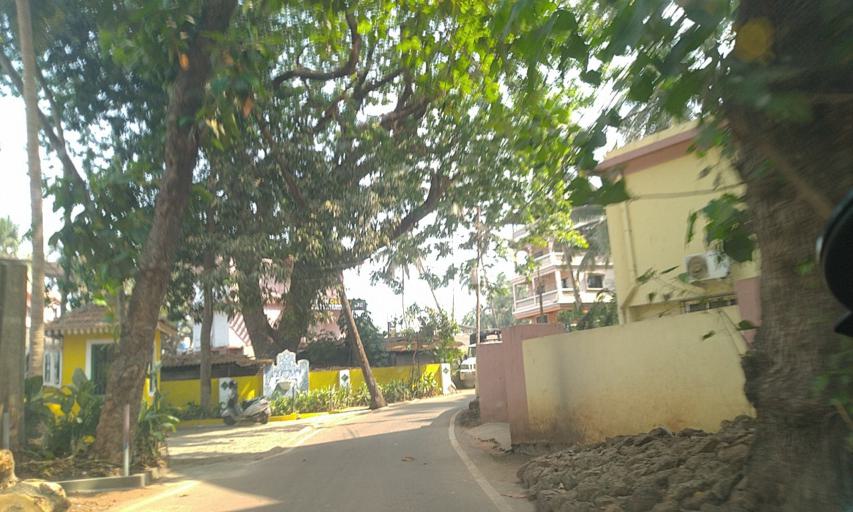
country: IN
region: Goa
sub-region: North Goa
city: Taleigao
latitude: 15.4774
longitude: 73.8444
